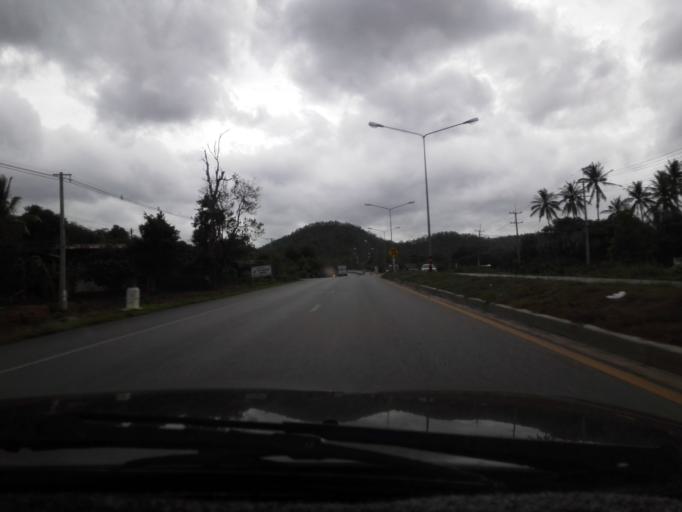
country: TH
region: Tak
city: Tak
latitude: 16.8200
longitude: 99.0731
